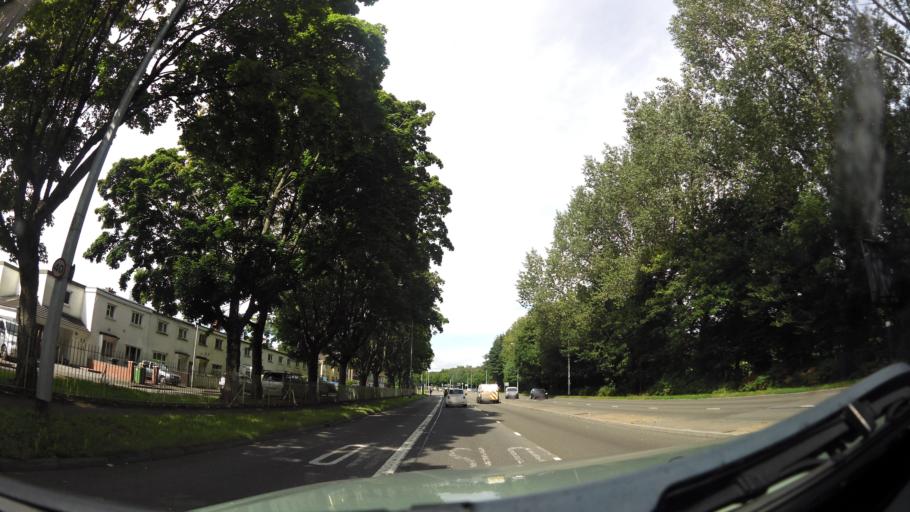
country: GB
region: Wales
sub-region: Cardiff
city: Radyr
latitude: 51.5228
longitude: -3.2278
